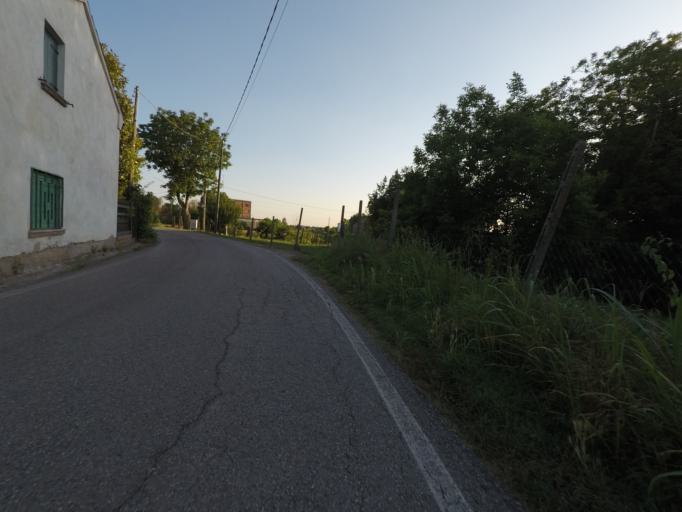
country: IT
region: Veneto
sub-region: Provincia di Rovigo
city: Fratta Polesine
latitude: 45.0381
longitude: 11.6414
